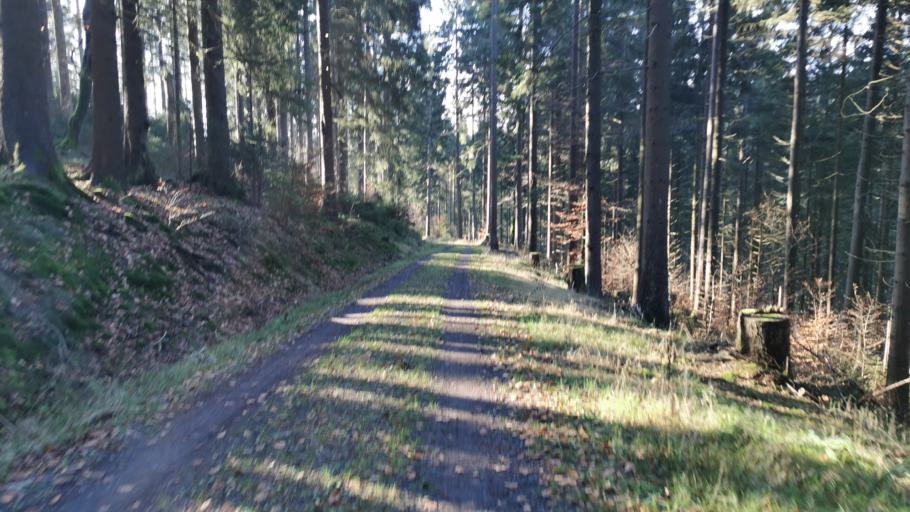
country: DE
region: Bavaria
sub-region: Upper Franconia
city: Tschirn
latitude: 50.4236
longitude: 11.4457
